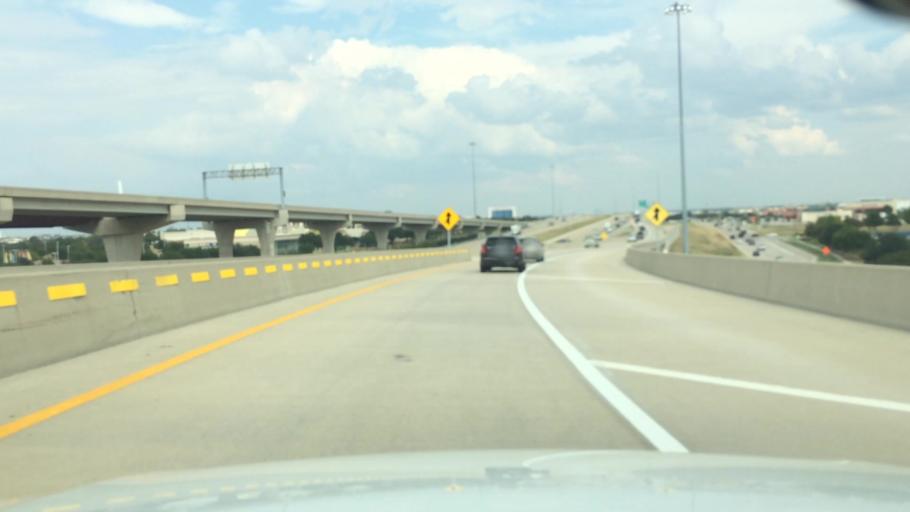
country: US
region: Texas
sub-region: Collin County
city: Frisco
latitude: 33.0910
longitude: -96.8213
